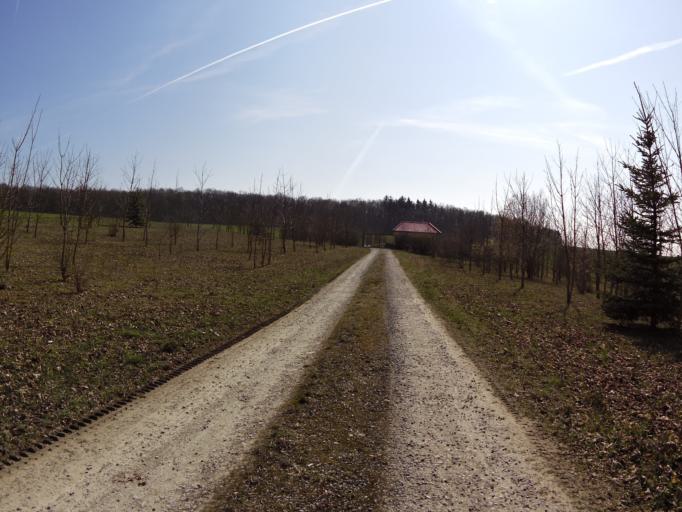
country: DE
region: Bavaria
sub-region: Regierungsbezirk Unterfranken
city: Estenfeld
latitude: 49.8114
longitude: 10.0131
